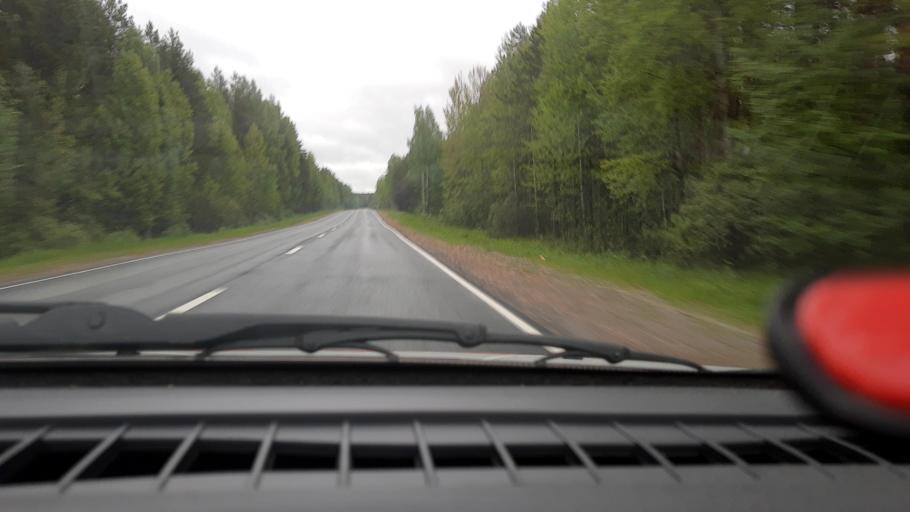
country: RU
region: Nizjnij Novgorod
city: Krasnyye Baki
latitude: 57.1688
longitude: 45.3140
